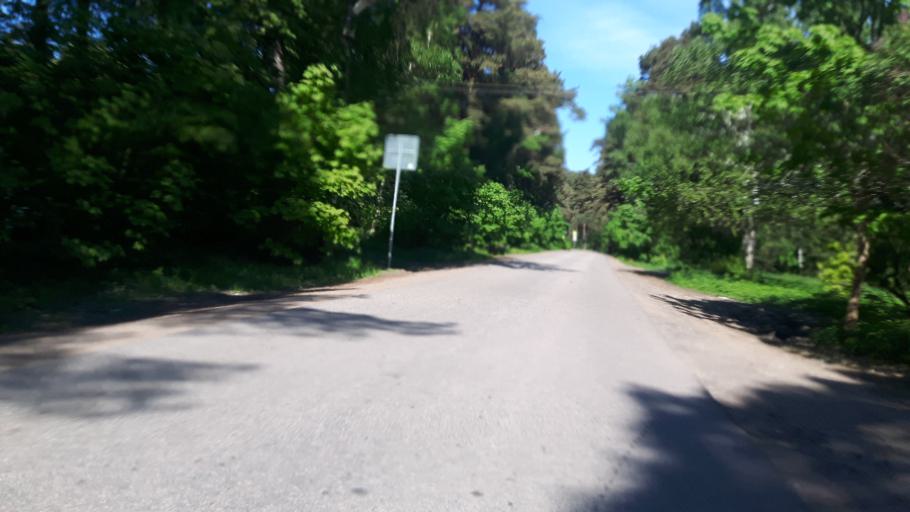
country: RU
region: Leningrad
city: Lebyazh'ye
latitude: 59.9633
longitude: 29.4107
